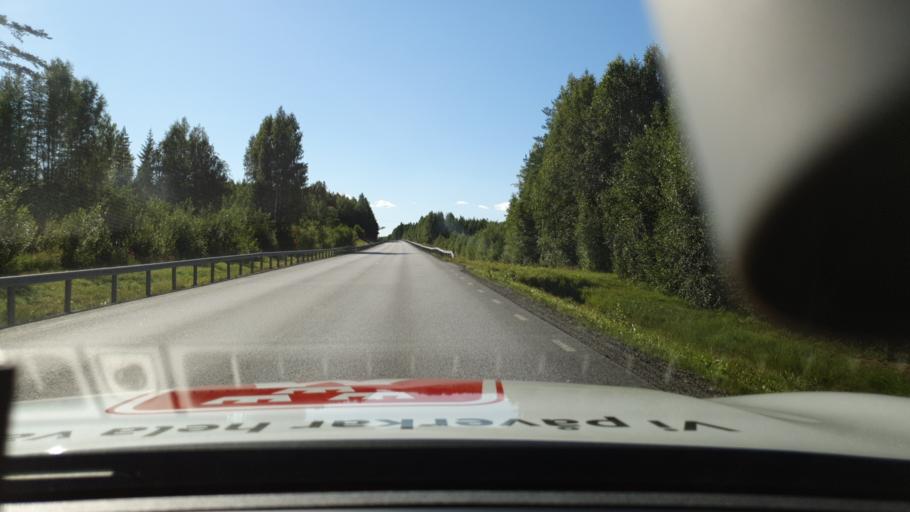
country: SE
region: Norrbotten
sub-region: Pitea Kommun
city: Rosvik
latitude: 65.5996
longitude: 21.5658
